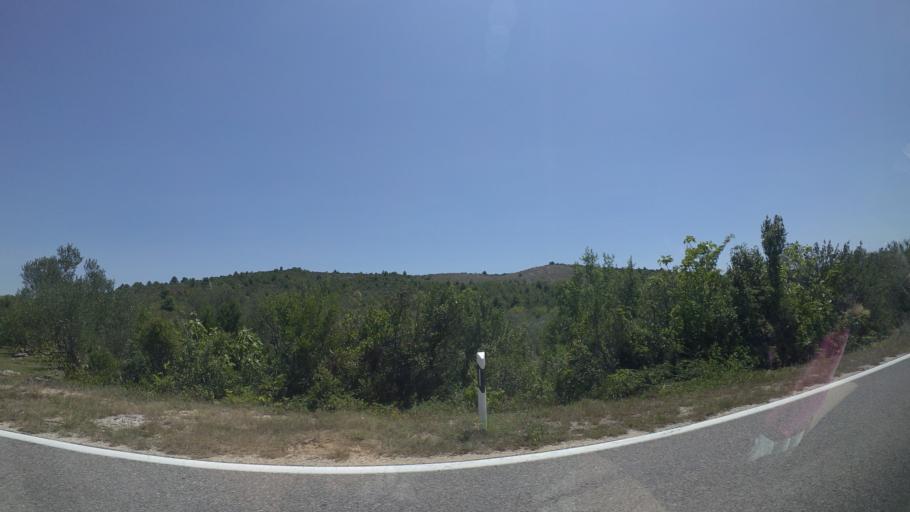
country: HR
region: Sibensko-Kniniska
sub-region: Grad Sibenik
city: Pirovac
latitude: 43.8056
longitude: 15.6999
